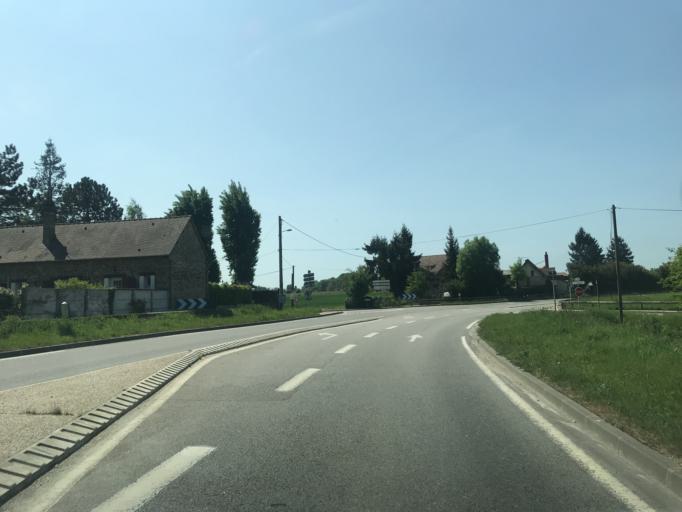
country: FR
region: Haute-Normandie
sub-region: Departement de l'Eure
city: Saint-Aubin-sur-Gaillon
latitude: 49.1208
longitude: 1.3105
